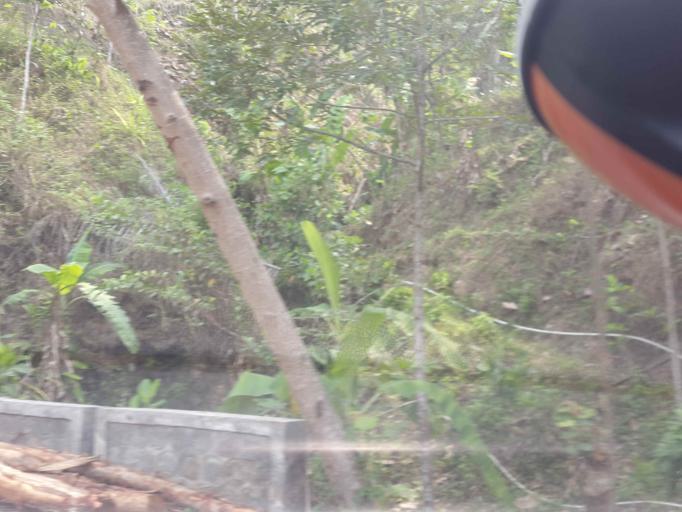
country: ID
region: East Java
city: Ploso
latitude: -8.0466
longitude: 111.1334
